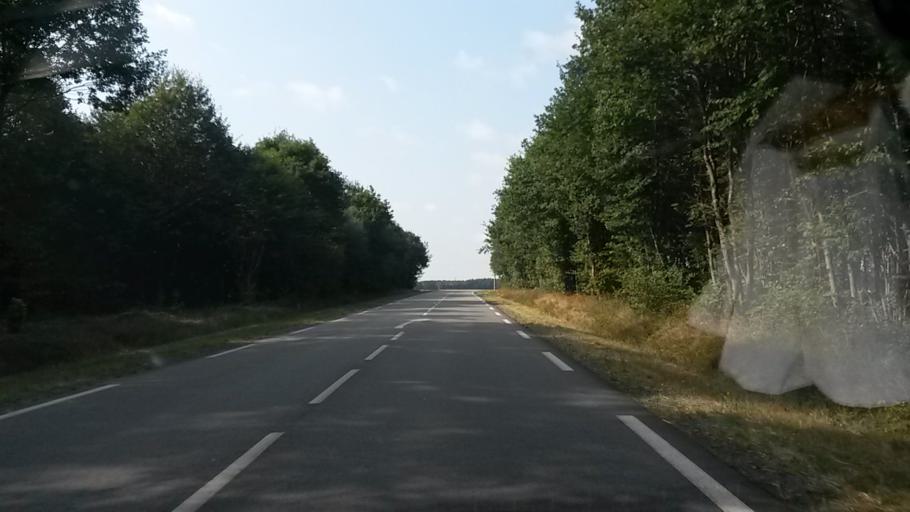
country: FR
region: Haute-Normandie
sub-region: Departement de l'Eure
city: Damville
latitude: 48.8545
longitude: 1.0612
